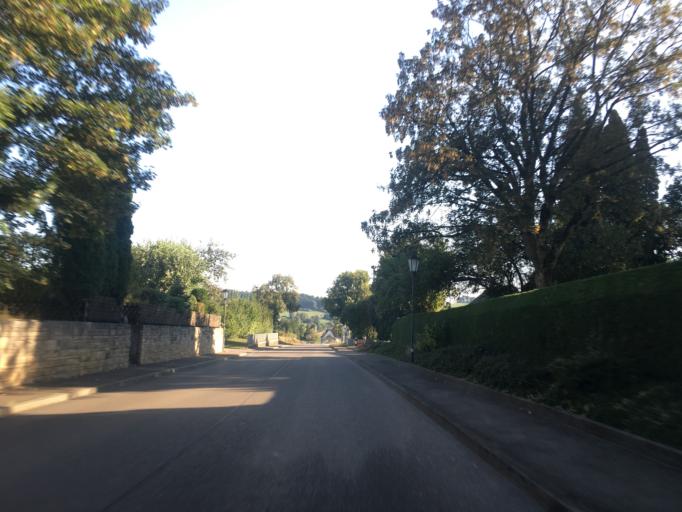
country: DE
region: Baden-Wuerttemberg
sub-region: Tuebingen Region
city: Hayingen
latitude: 48.2731
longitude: 9.4751
